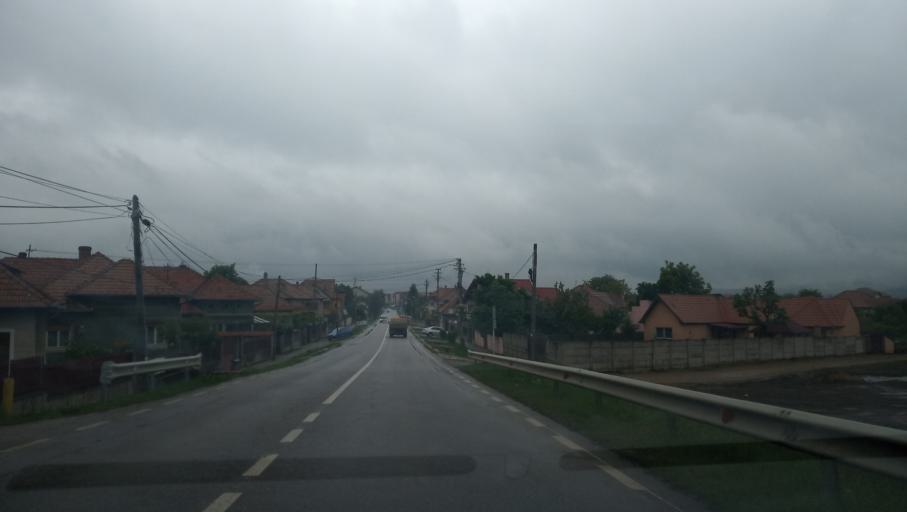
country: RO
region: Alba
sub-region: Municipiul Sebes
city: Sebes
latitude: 45.9505
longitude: 23.5830
